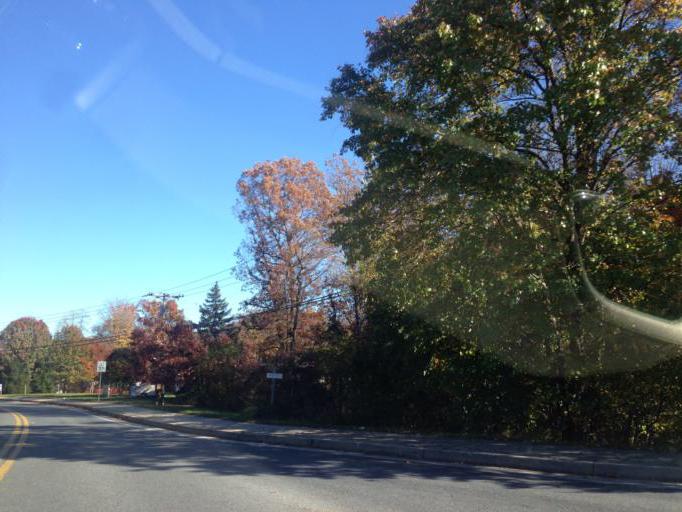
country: US
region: Maryland
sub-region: Howard County
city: Riverside
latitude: 39.1983
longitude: -76.8840
